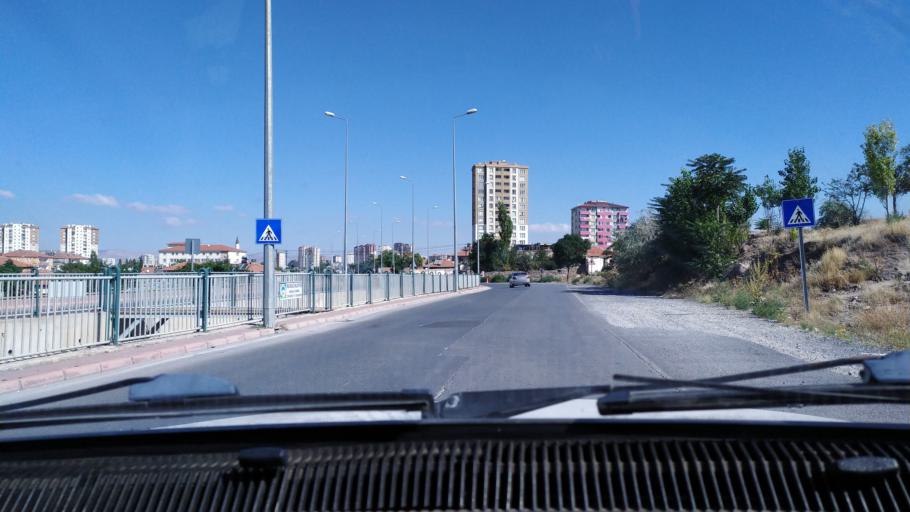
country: TR
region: Kayseri
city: Talas
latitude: 38.7265
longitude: 35.5507
